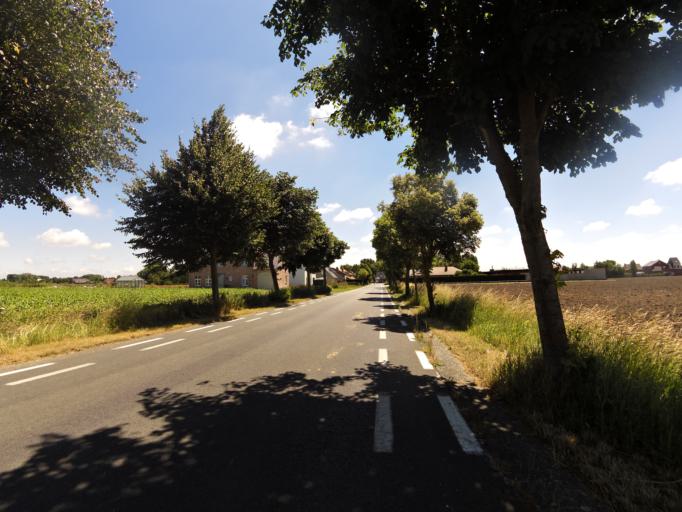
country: BE
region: Flanders
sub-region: Provincie West-Vlaanderen
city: Ichtegem
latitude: 51.1112
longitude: 3.0433
